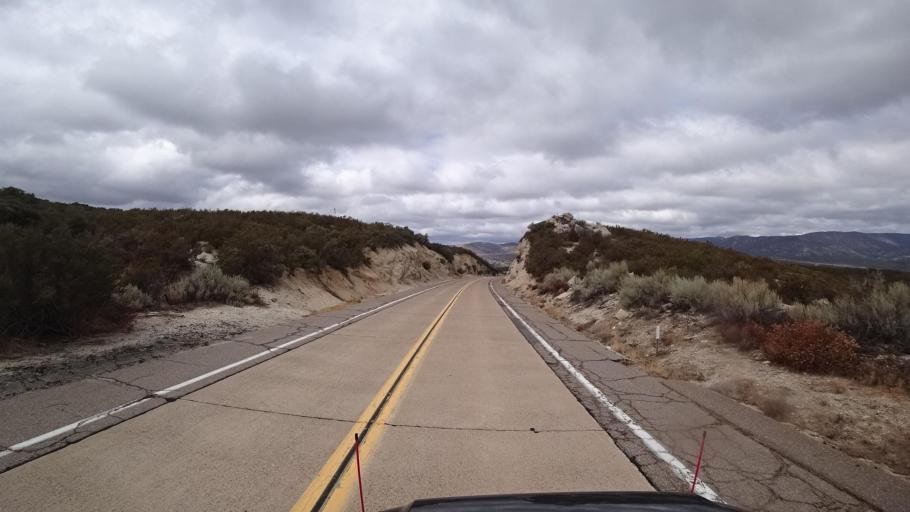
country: US
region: California
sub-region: San Diego County
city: Campo
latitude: 32.7201
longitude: -116.4063
